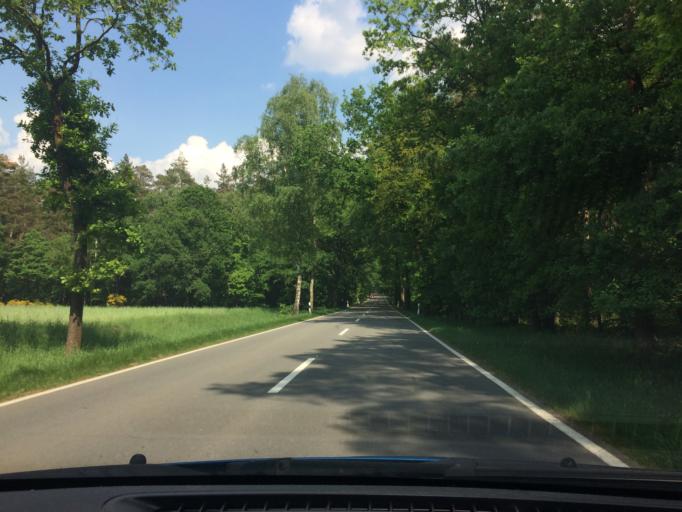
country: DE
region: Lower Saxony
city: Tosterglope
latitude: 53.2170
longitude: 10.8507
